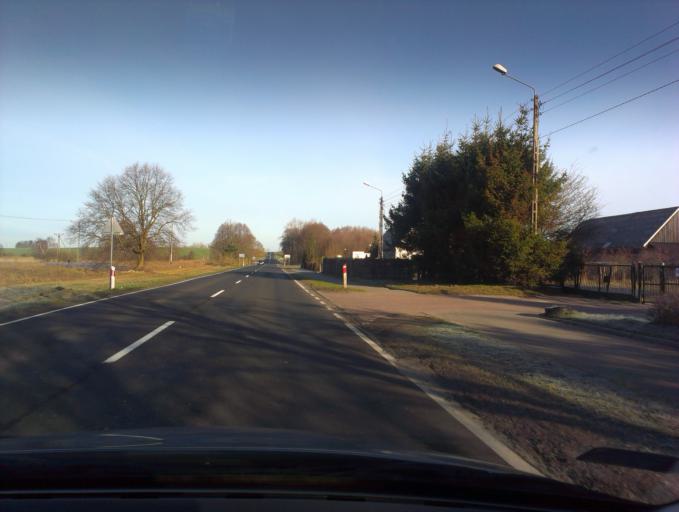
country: PL
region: West Pomeranian Voivodeship
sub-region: Powiat koszalinski
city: Sianow
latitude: 54.1344
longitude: 16.2842
